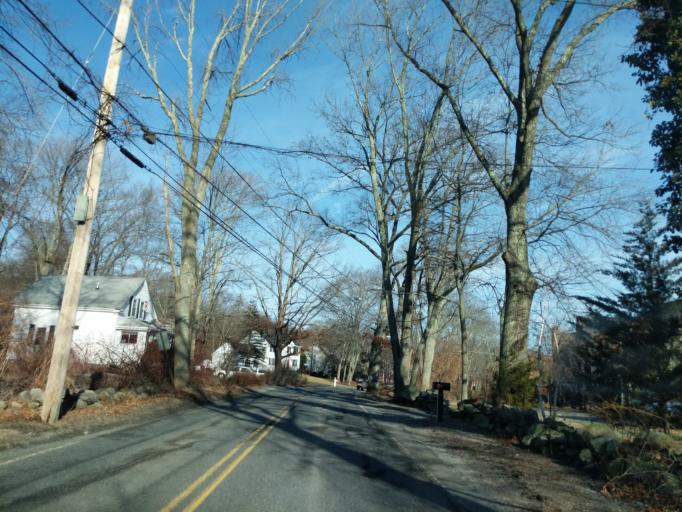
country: US
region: Massachusetts
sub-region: Worcester County
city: Blackstone
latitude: 42.0266
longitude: -71.5525
